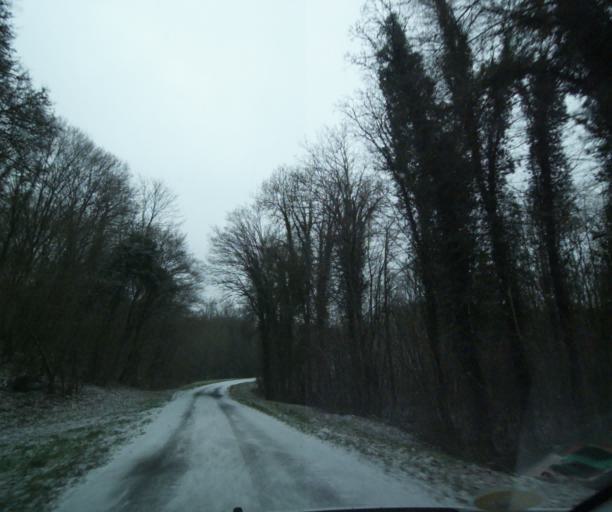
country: FR
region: Champagne-Ardenne
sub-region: Departement de la Haute-Marne
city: Bienville
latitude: 48.4830
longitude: 5.0471
